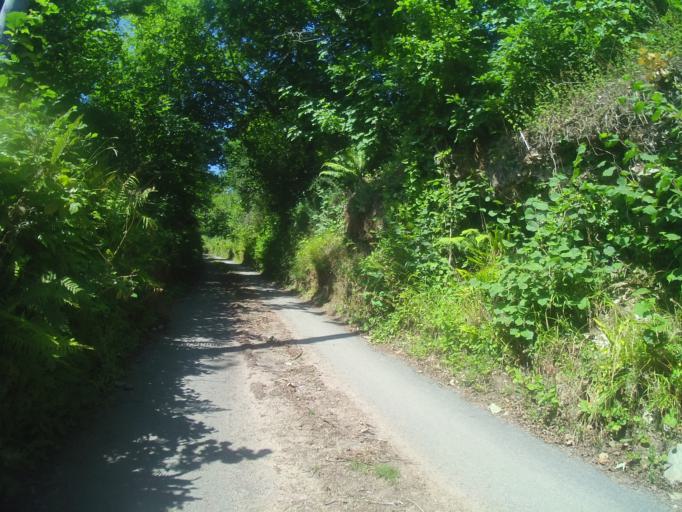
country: GB
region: England
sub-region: Devon
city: Dartmouth
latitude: 50.3584
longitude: -3.6152
